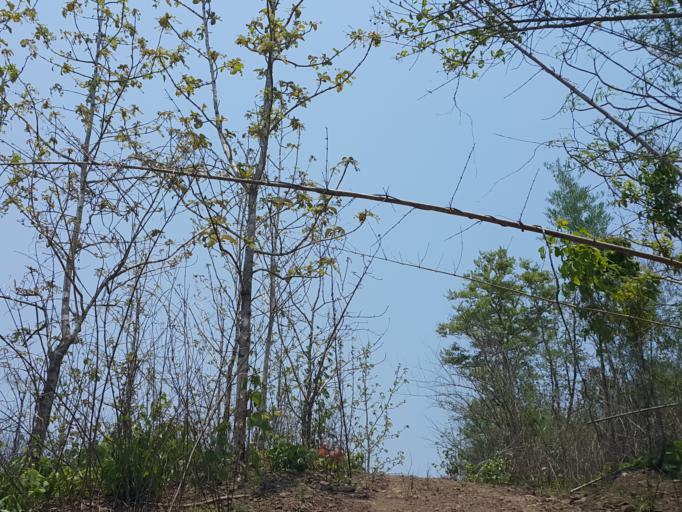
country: TH
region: Kanchanaburi
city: Sai Yok
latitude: 14.2385
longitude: 98.8711
